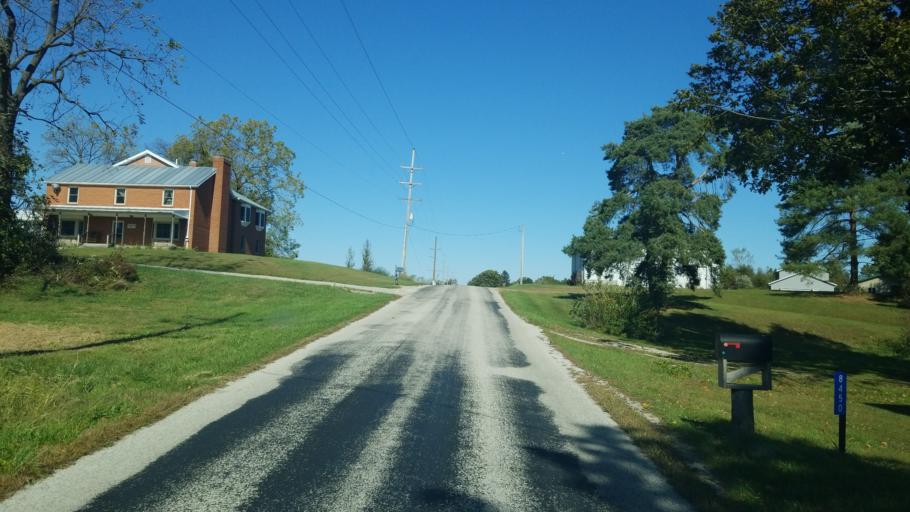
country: US
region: Ohio
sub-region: Huron County
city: Plymouth
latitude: 40.9909
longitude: -82.6961
